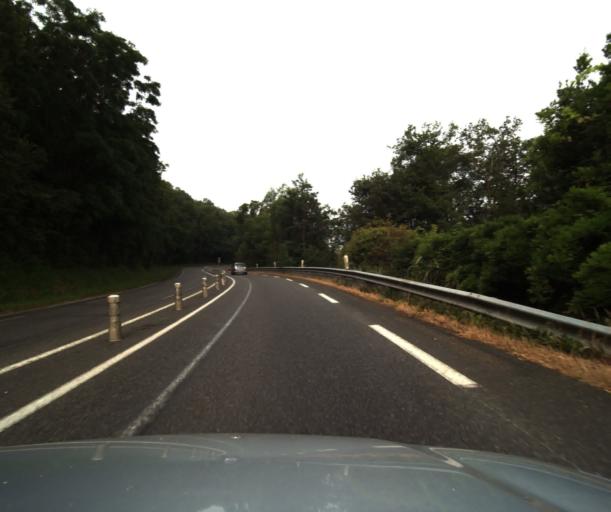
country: FR
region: Midi-Pyrenees
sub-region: Departement du Gers
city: Mirande
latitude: 43.5486
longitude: 0.4803
